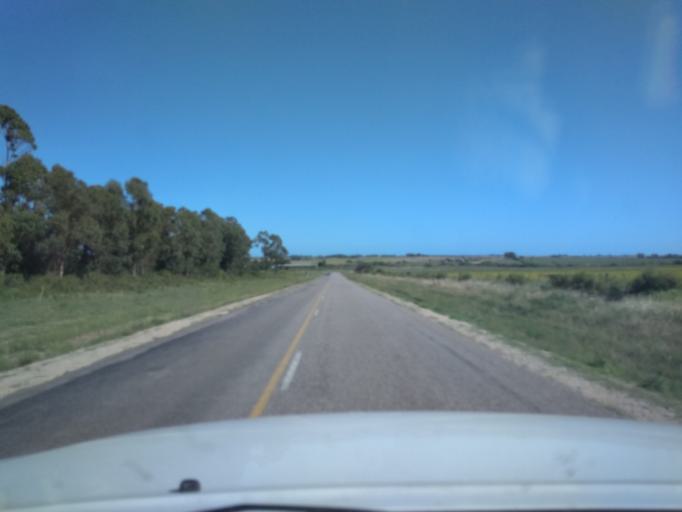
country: UY
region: Canelones
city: San Ramon
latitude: -34.2271
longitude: -55.9298
